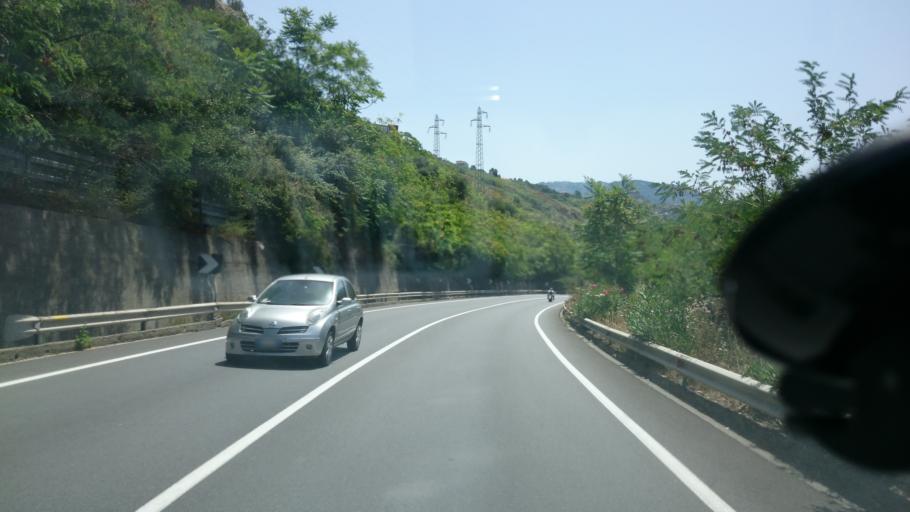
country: IT
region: Calabria
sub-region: Provincia di Cosenza
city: Cetraro Marina
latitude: 39.5298
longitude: 15.9237
